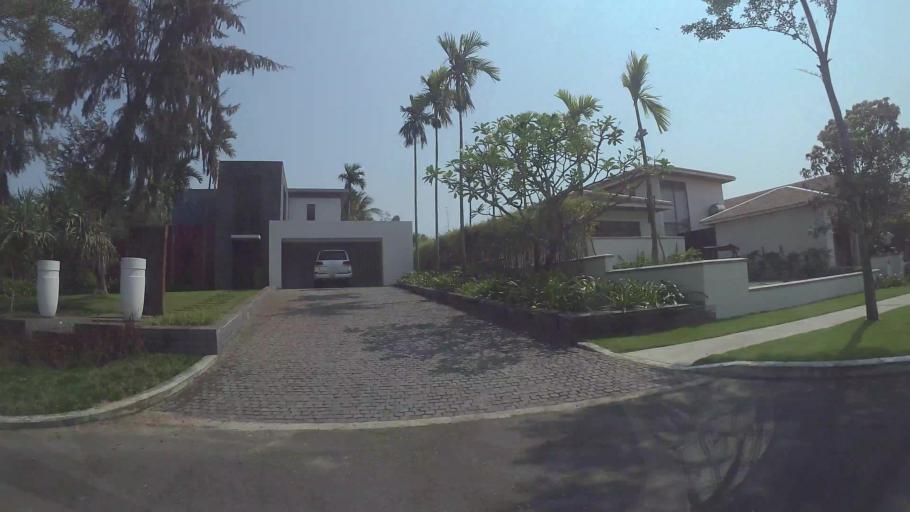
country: VN
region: Da Nang
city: Ngu Hanh Son
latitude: 15.9794
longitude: 108.2784
